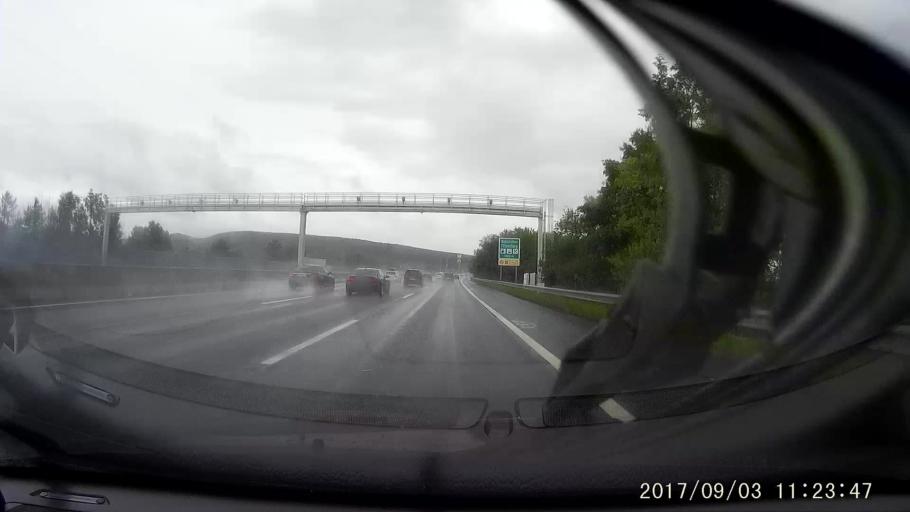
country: AT
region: Lower Austria
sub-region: Politischer Bezirk Wiener Neustadt
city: Weikersdorf am Steinfelde
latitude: 47.8278
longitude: 16.1849
